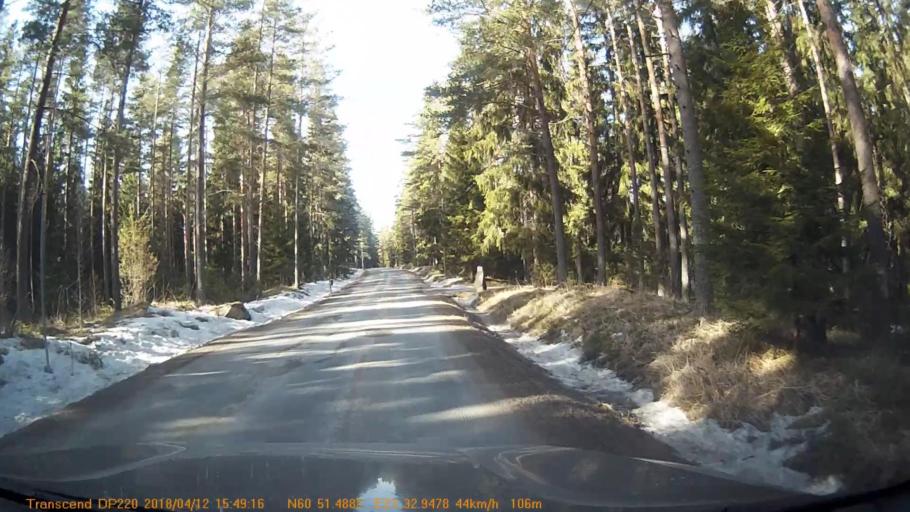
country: FI
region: Haeme
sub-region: Forssa
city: Forssa
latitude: 60.8584
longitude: 23.5490
